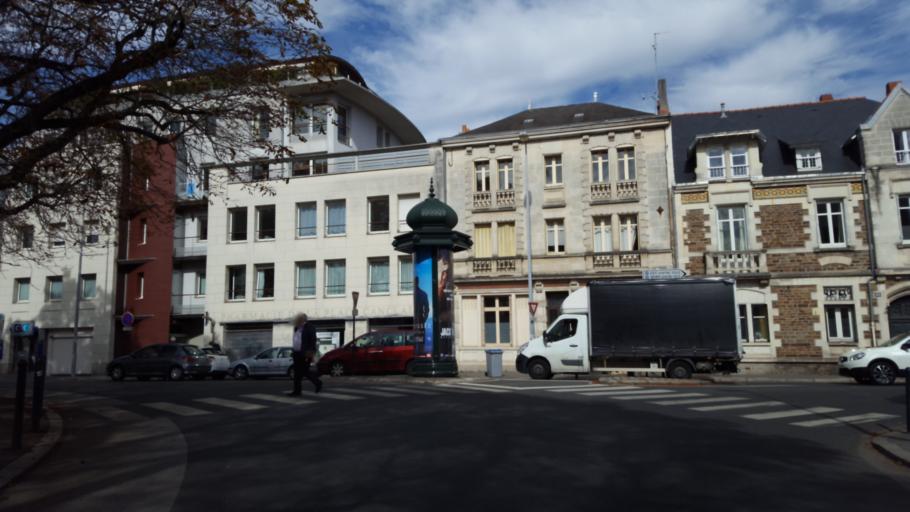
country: FR
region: Pays de la Loire
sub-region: Departement de la Loire-Atlantique
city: Nantes
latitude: 47.2144
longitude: -1.5742
